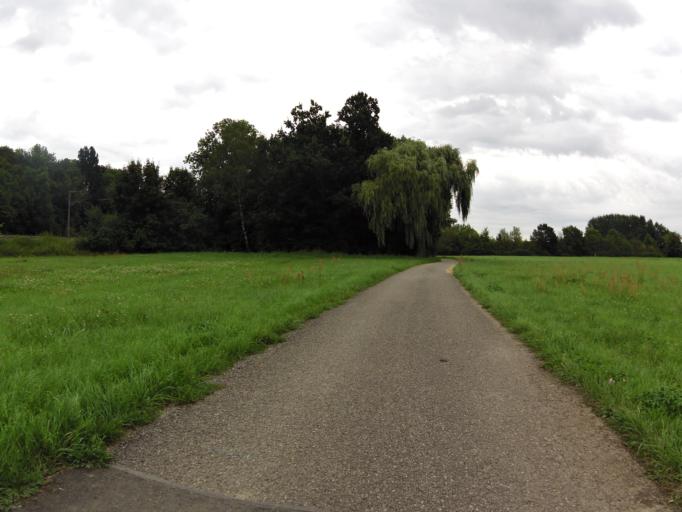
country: DE
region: Bavaria
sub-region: Regierungsbezirk Unterfranken
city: Wonfurt
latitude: 50.0182
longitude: 10.4550
